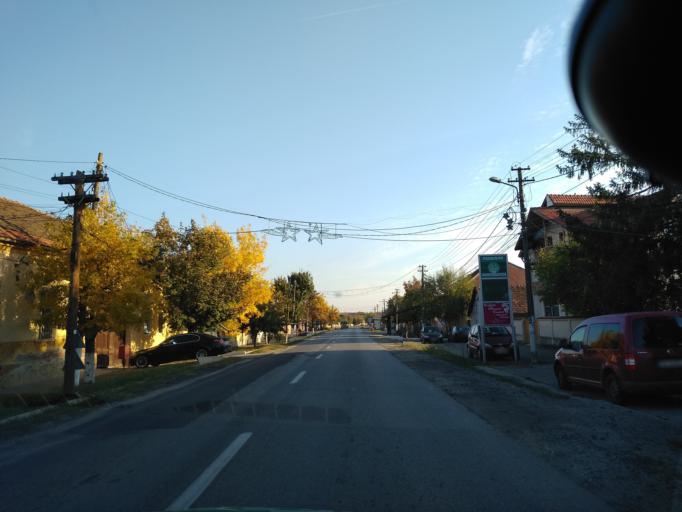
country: RO
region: Timis
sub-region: Comuna Pischia
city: Pischia
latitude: 45.9045
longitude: 21.3403
